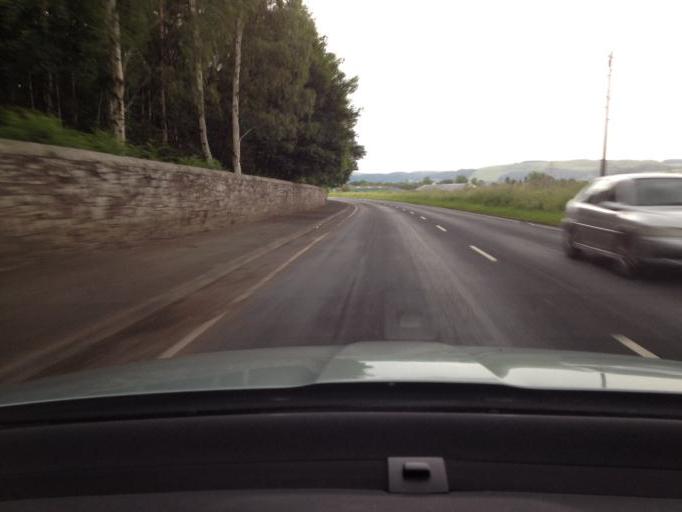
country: GB
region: Scotland
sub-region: Perth and Kinross
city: Bridge of Earn
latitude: 56.3580
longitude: -3.4140
